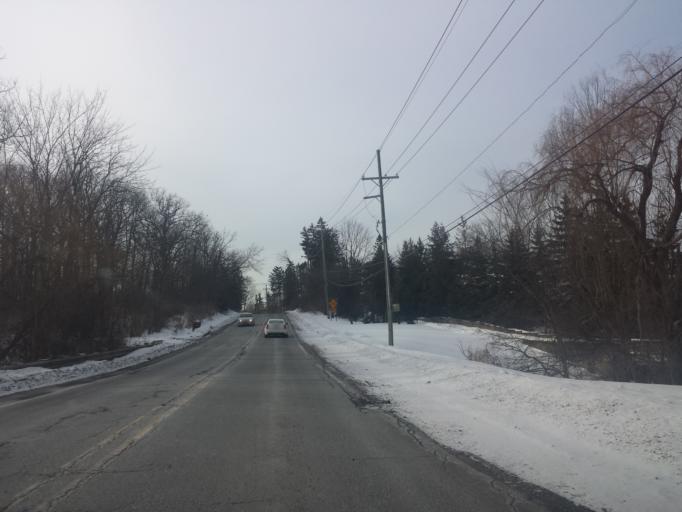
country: US
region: Michigan
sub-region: Oakland County
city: Orchard Lake
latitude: 42.5623
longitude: -83.3412
